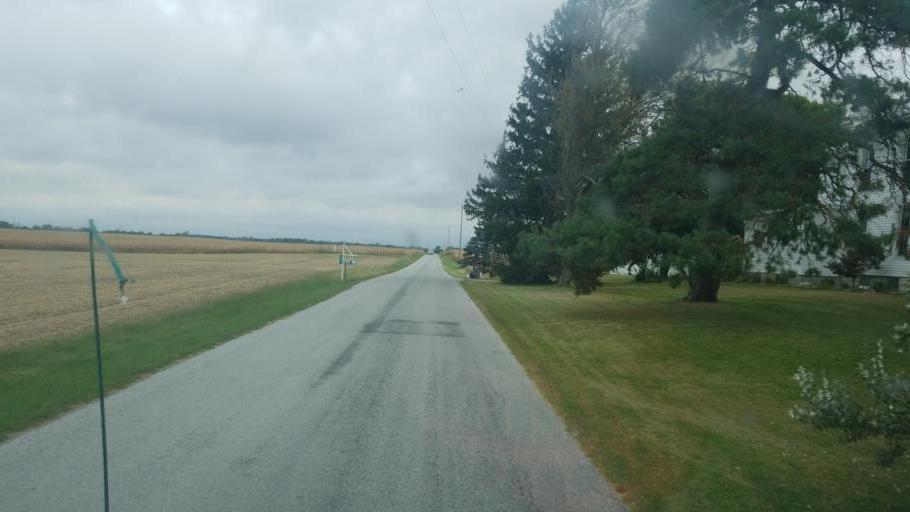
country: US
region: Ohio
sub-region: Seneca County
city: Fostoria
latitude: 41.0561
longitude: -83.4961
